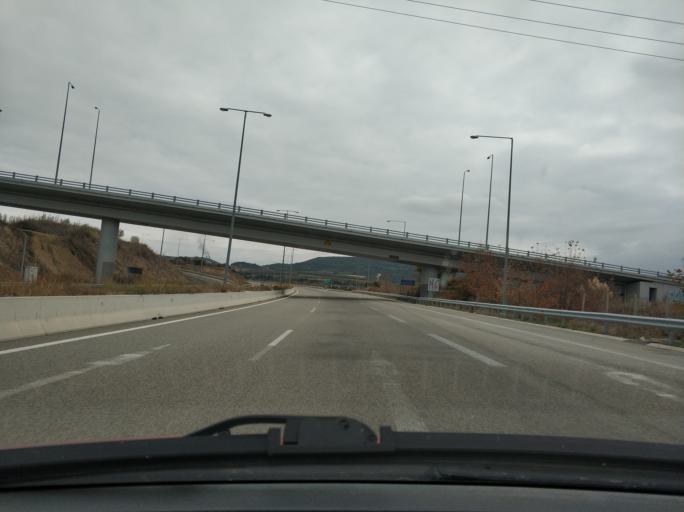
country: GR
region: East Macedonia and Thrace
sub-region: Nomos Kavalas
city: Paralia Ofryniou
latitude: 40.7852
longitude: 23.9549
